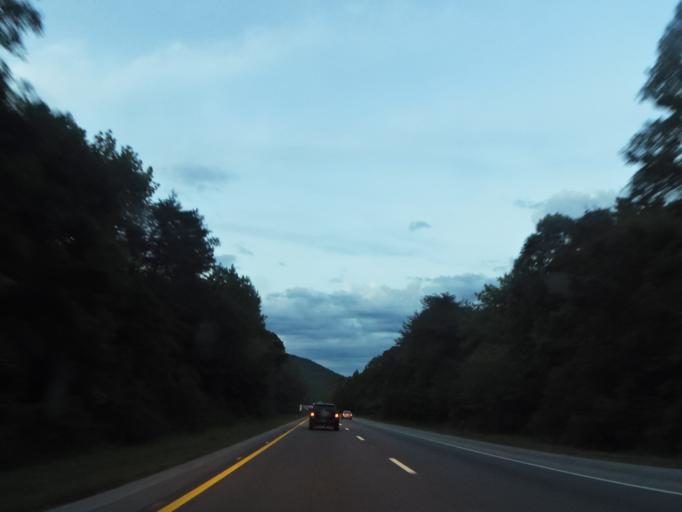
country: US
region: Tennessee
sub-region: Roane County
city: Midtown
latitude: 35.9060
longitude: -84.6177
